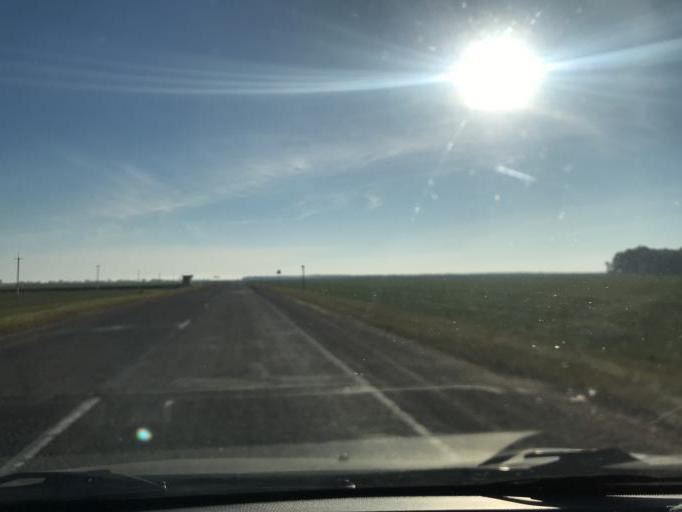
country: BY
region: Gomel
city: Brahin
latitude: 51.7928
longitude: 30.1667
